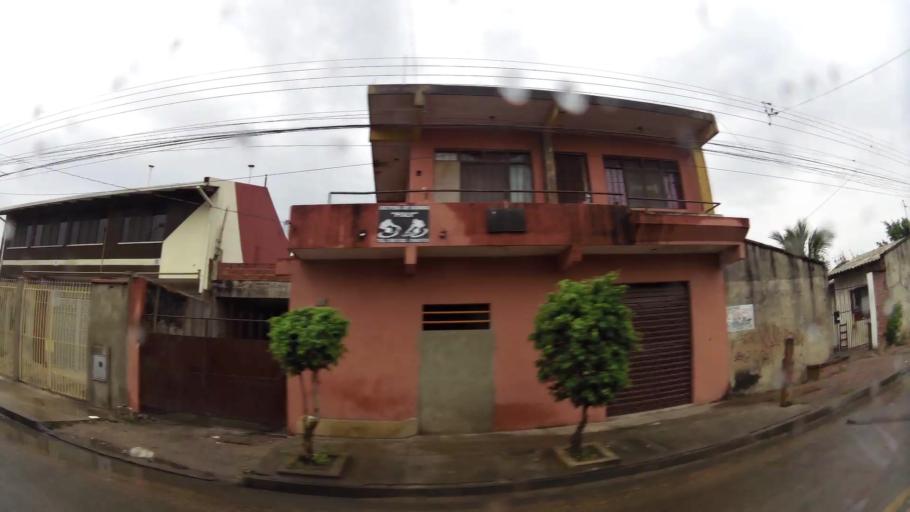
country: BO
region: Santa Cruz
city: Santa Cruz de la Sierra
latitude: -17.7584
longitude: -63.1191
